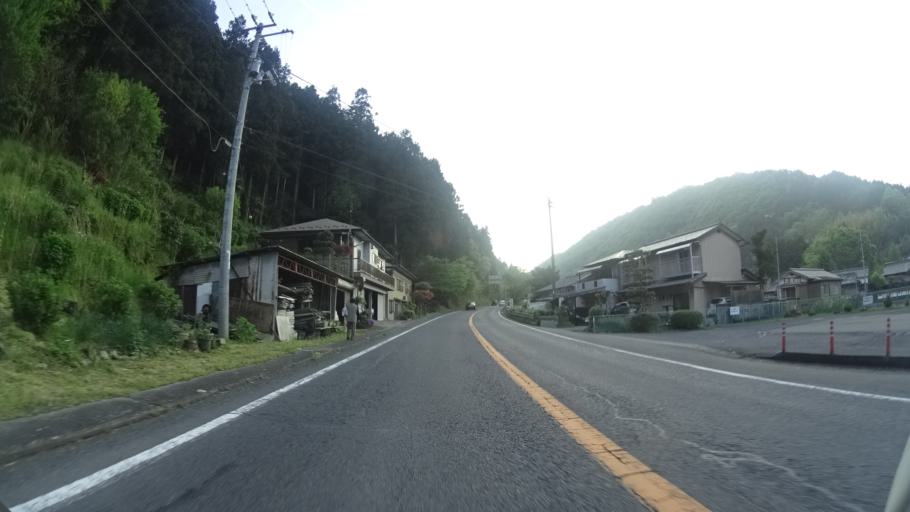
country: JP
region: Tokushima
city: Ikedacho
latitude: 34.0016
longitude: 133.7050
